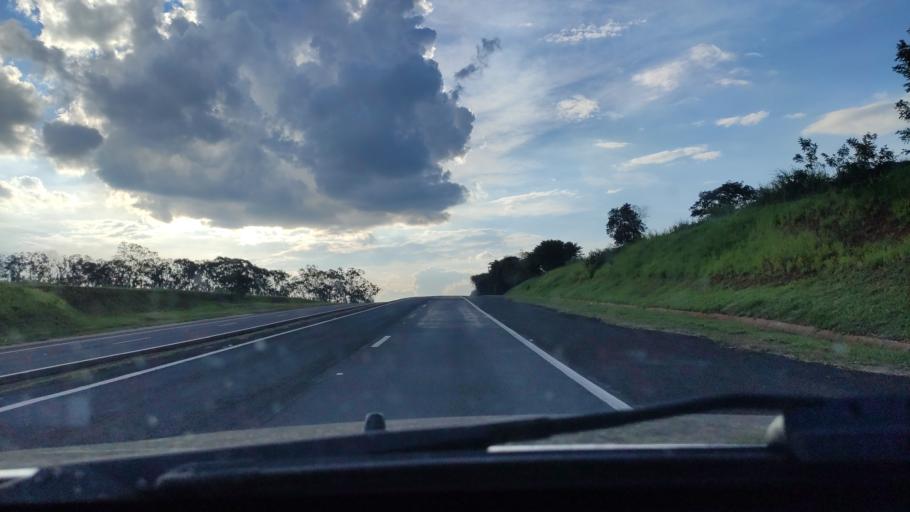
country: BR
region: Sao Paulo
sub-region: Maracai
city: Maracai
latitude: -22.4963
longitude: -50.9034
